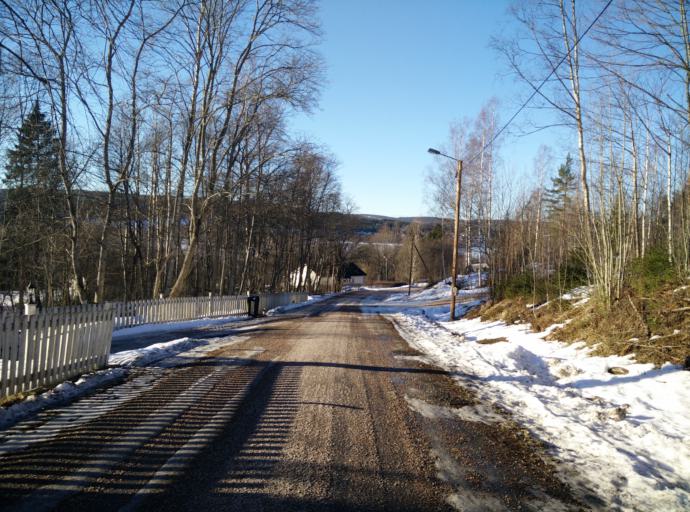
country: SE
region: Vaesternorrland
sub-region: Sundsvalls Kommun
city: Skottsund
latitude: 62.3129
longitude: 17.3979
